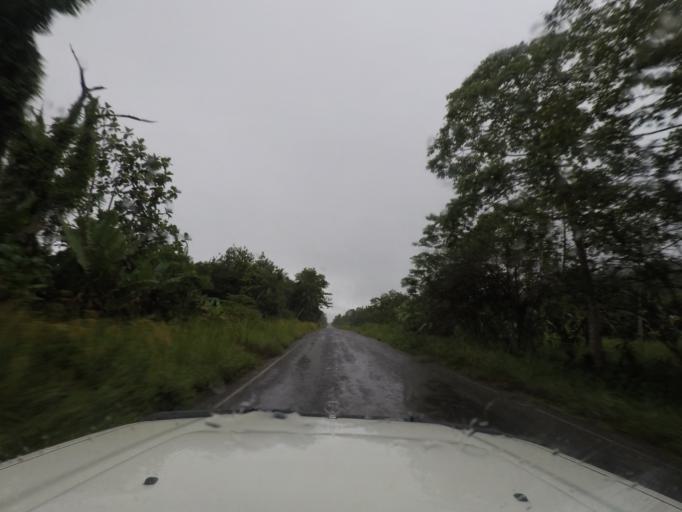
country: PG
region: Madang
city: Madang
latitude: -5.3857
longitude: 145.6901
